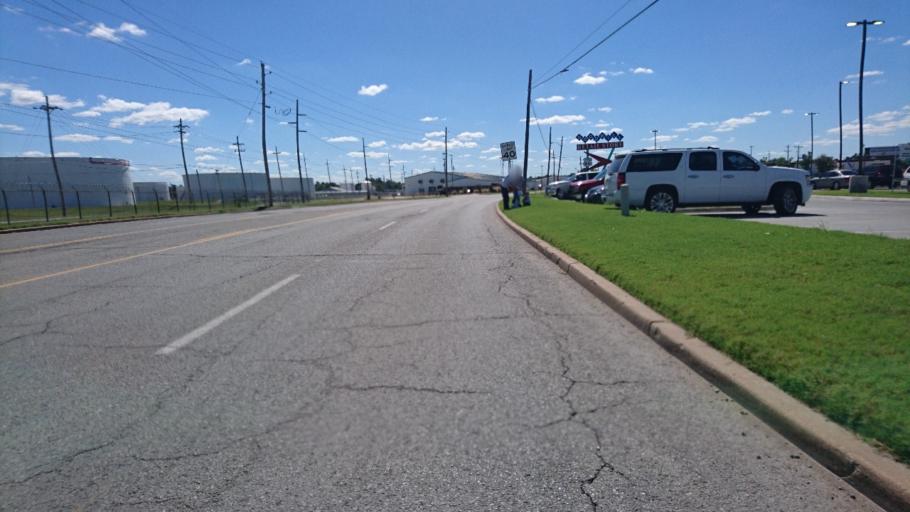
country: US
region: Oklahoma
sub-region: Tulsa County
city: Tulsa
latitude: 36.1184
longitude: -96.0072
